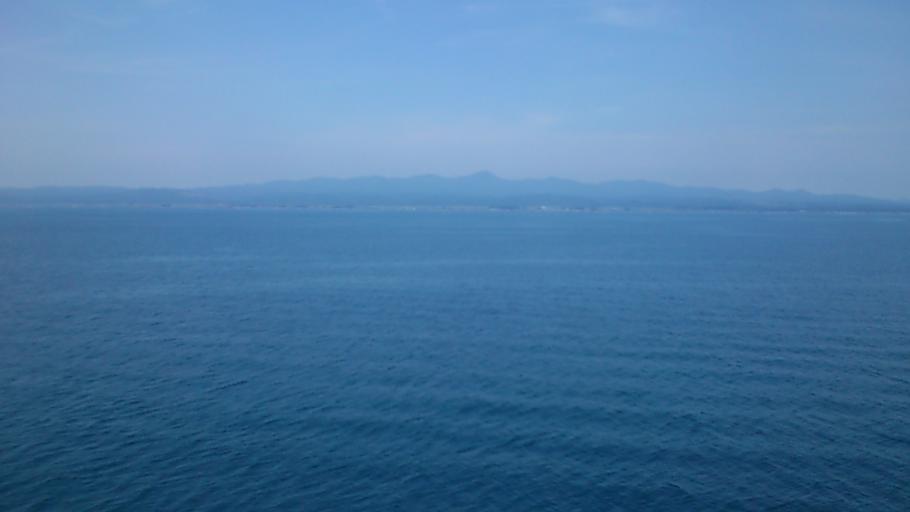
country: JP
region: Aomori
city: Aomori Shi
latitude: 40.9600
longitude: 140.7328
